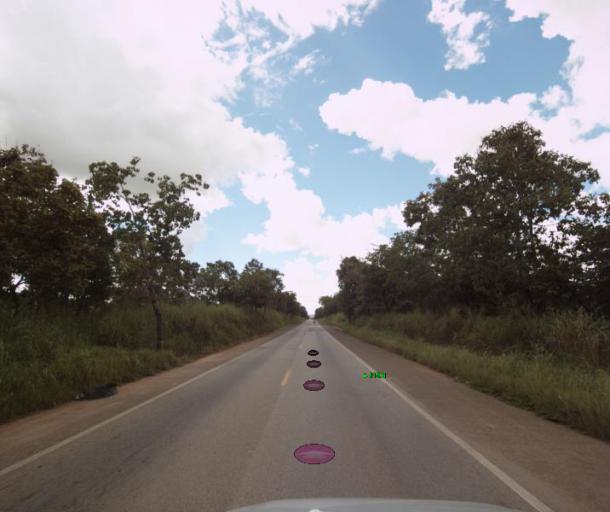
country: BR
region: Goias
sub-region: Porangatu
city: Porangatu
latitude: -13.7873
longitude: -49.0339
